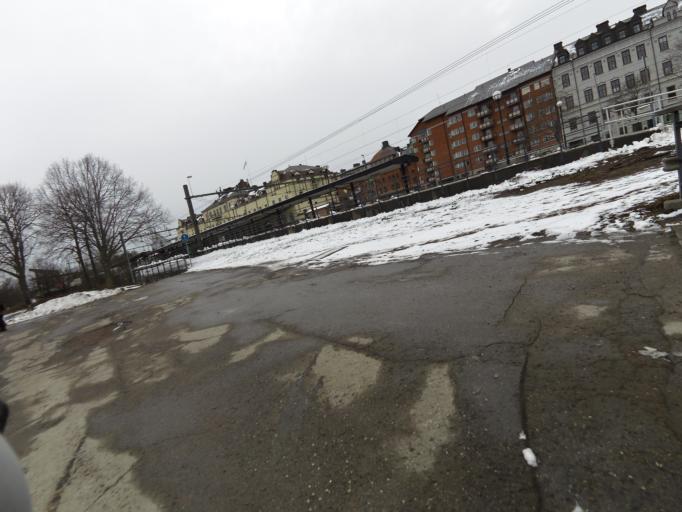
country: SE
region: Gaevleborg
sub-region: Gavle Kommun
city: Gavle
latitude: 60.6771
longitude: 17.1508
